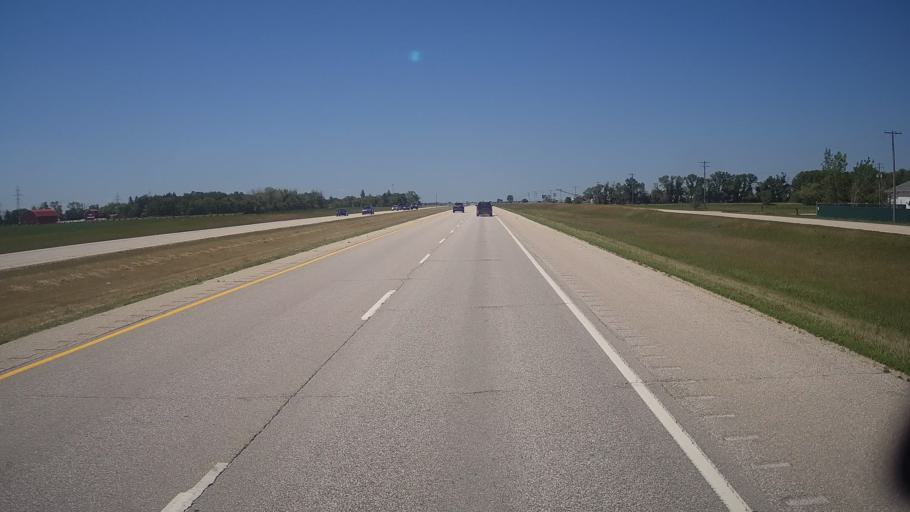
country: CA
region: Manitoba
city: Stonewall
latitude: 49.9900
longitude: -97.2652
